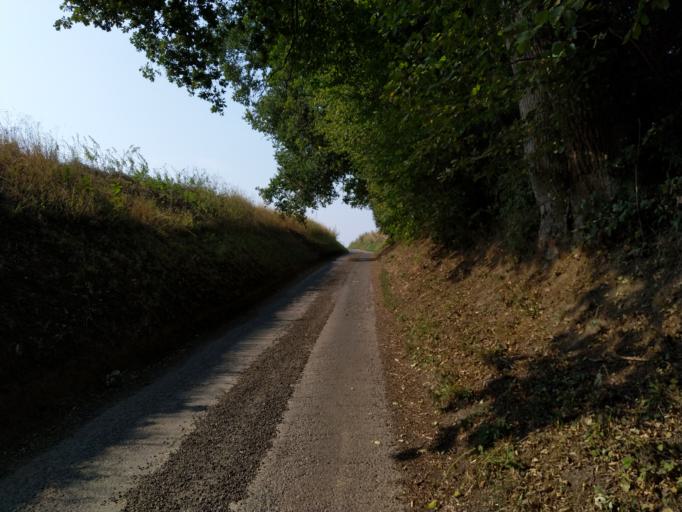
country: BE
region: Wallonia
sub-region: Province du Hainaut
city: Seneffe
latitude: 50.5521
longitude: 4.2794
